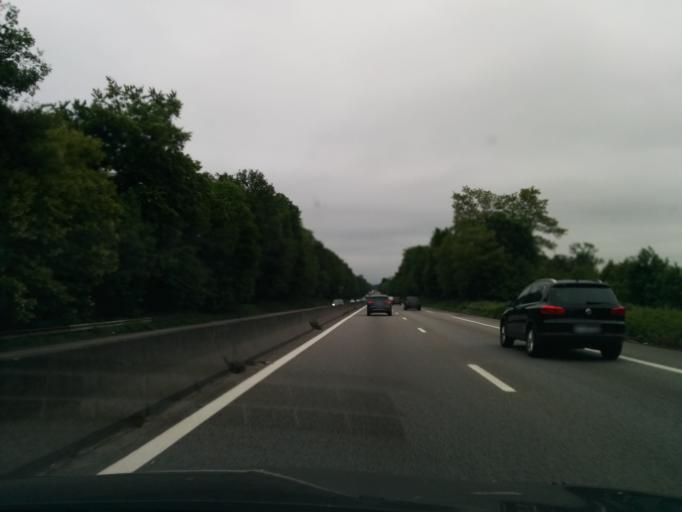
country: FR
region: Ile-de-France
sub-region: Departement des Yvelines
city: Saint-Nom-la-Breteche
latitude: 48.8656
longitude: 2.0369
